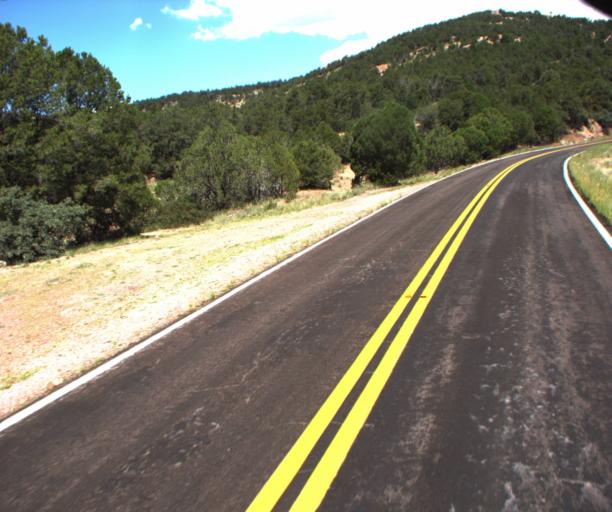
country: US
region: Arizona
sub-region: Greenlee County
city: Morenci
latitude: 33.3880
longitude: -109.3324
